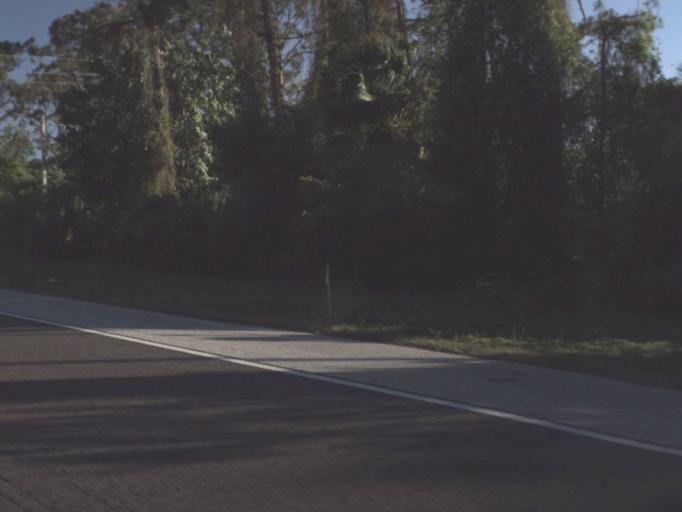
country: US
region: Florida
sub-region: Flagler County
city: Flagler Beach
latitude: 29.4092
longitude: -81.1578
